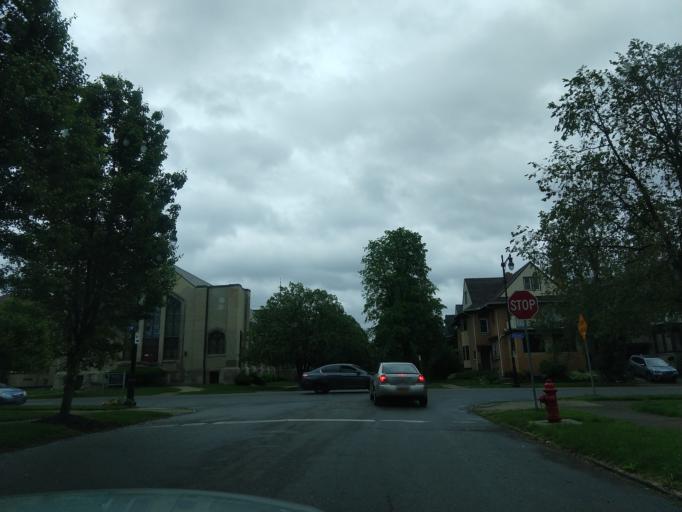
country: US
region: New York
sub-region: Erie County
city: Buffalo
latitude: 42.9169
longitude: -78.8824
